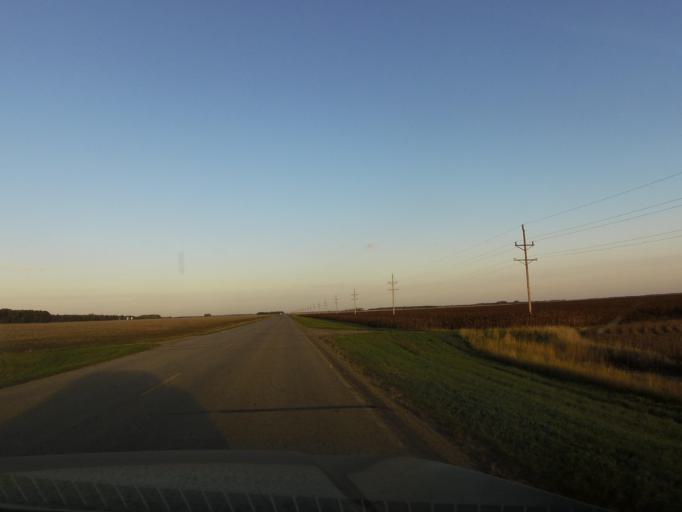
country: CA
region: Manitoba
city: Altona
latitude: 48.9633
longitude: -97.6349
